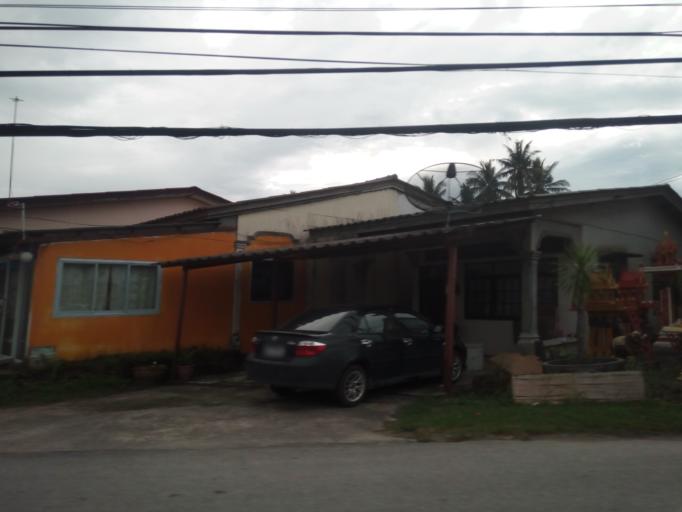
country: TH
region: Phuket
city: Thalang
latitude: 7.9980
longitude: 98.3495
